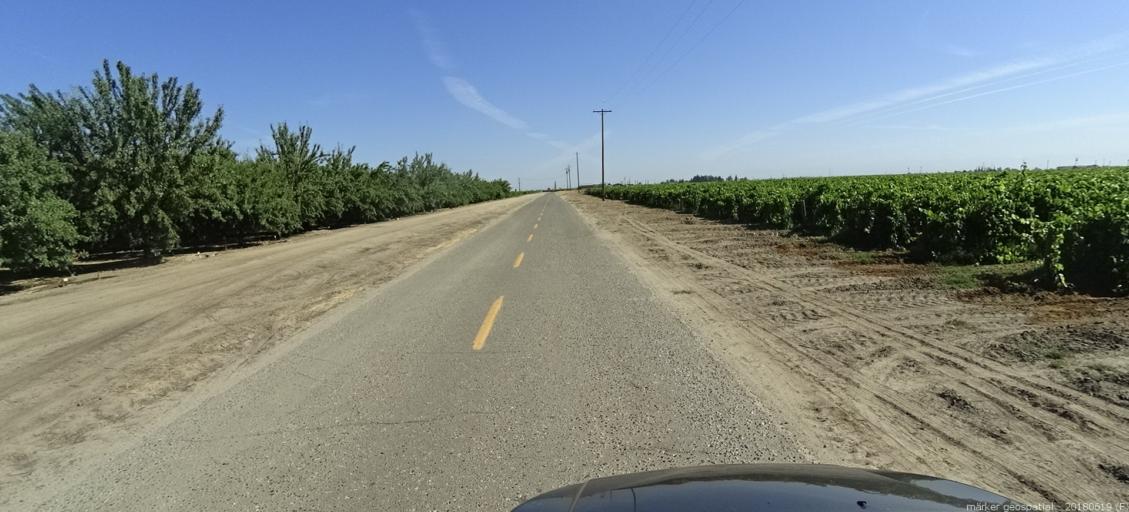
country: US
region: California
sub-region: Fresno County
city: Biola
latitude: 36.8315
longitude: -120.0789
